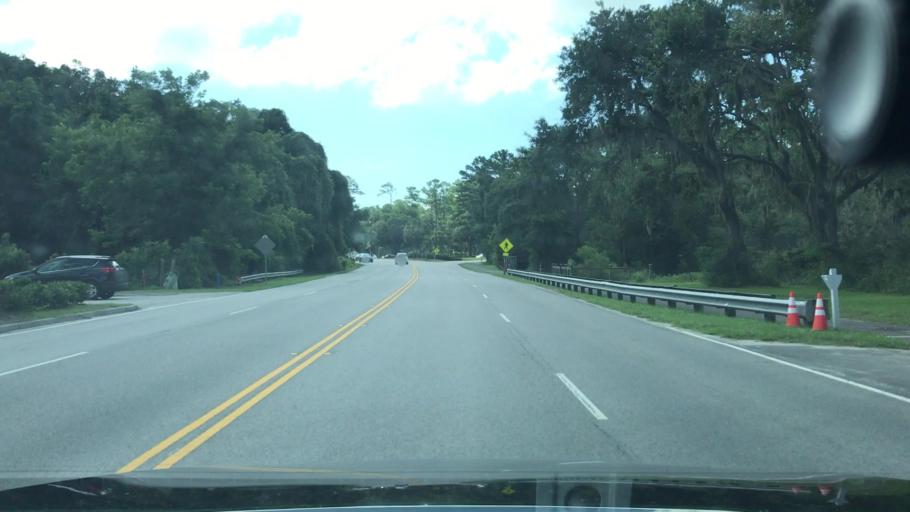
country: US
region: South Carolina
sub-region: Beaufort County
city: Hilton Head Island
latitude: 32.2038
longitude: -80.7006
